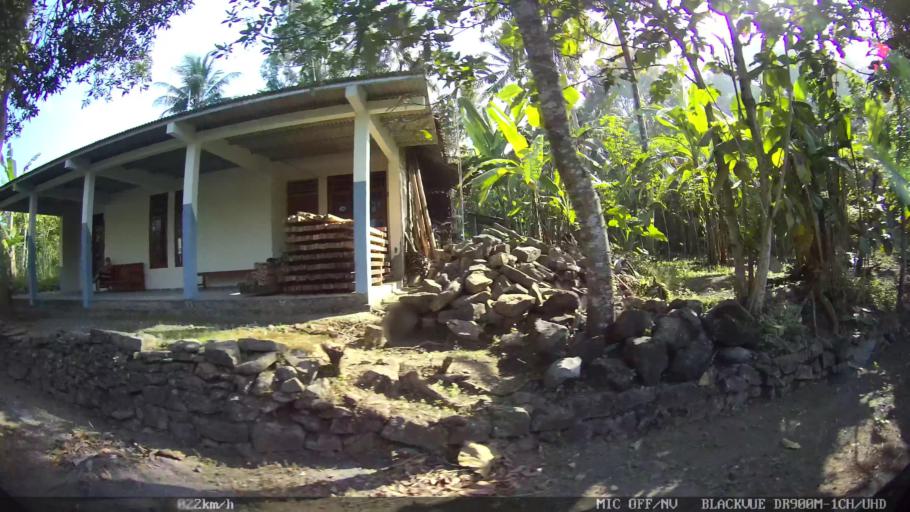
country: ID
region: Daerah Istimewa Yogyakarta
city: Kasihan
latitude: -7.8328
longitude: 110.2737
